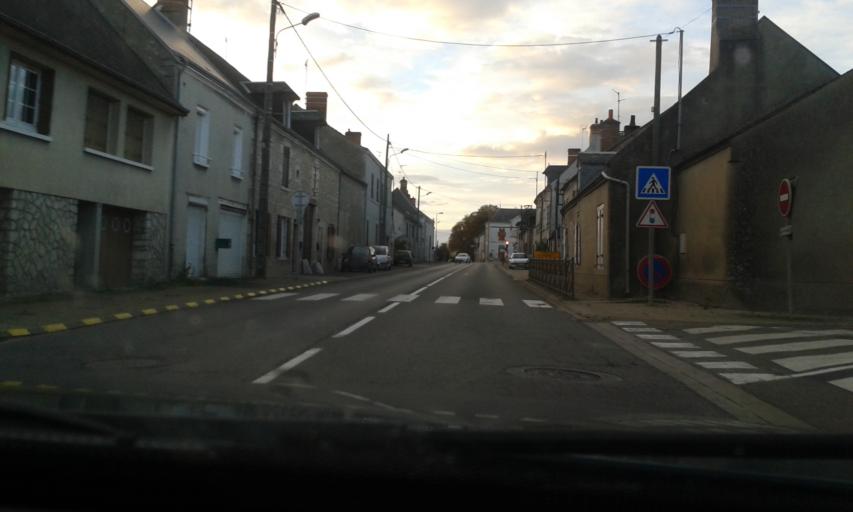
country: FR
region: Centre
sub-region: Departement du Loiret
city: Patay
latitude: 47.9993
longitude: 1.7015
